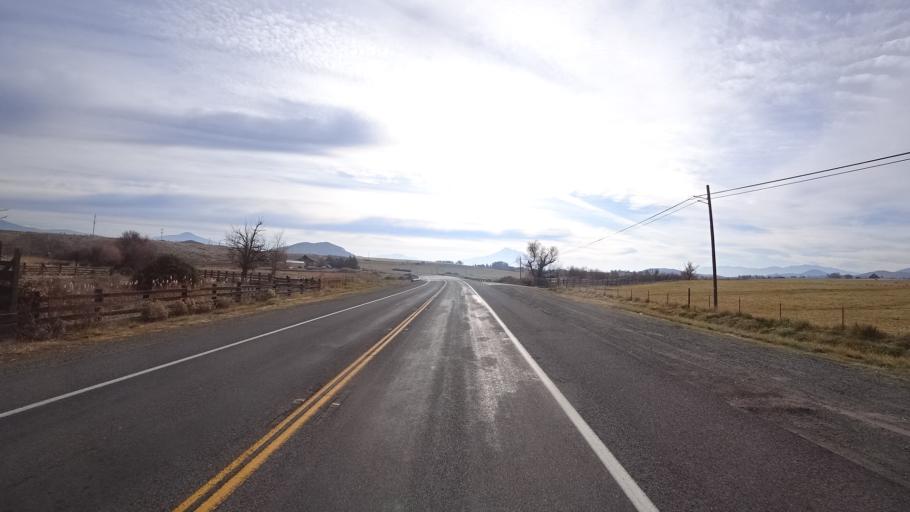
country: US
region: California
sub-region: Siskiyou County
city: Montague
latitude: 41.7270
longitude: -122.5594
